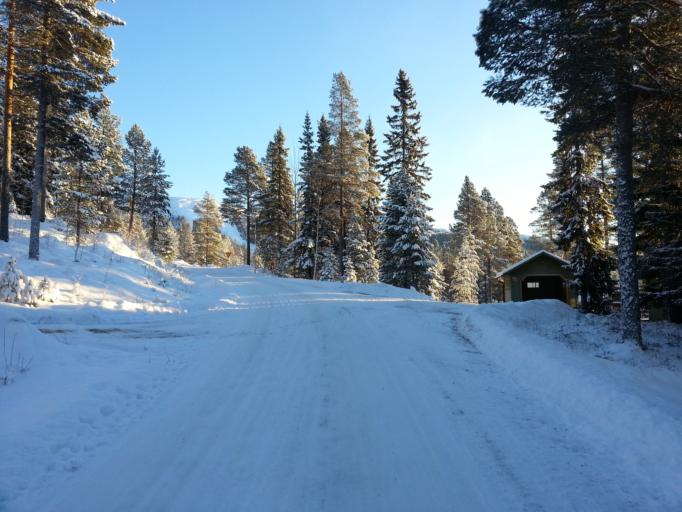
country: SE
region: Jaemtland
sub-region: Harjedalens Kommun
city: Sveg
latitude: 62.4242
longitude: 13.9466
